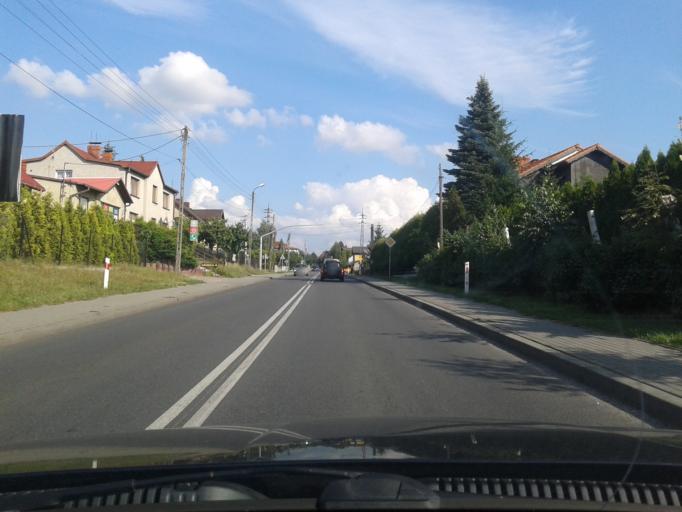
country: PL
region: Silesian Voivodeship
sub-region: Powiat wodzislawski
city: Gorzyce
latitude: 49.9598
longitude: 18.3928
